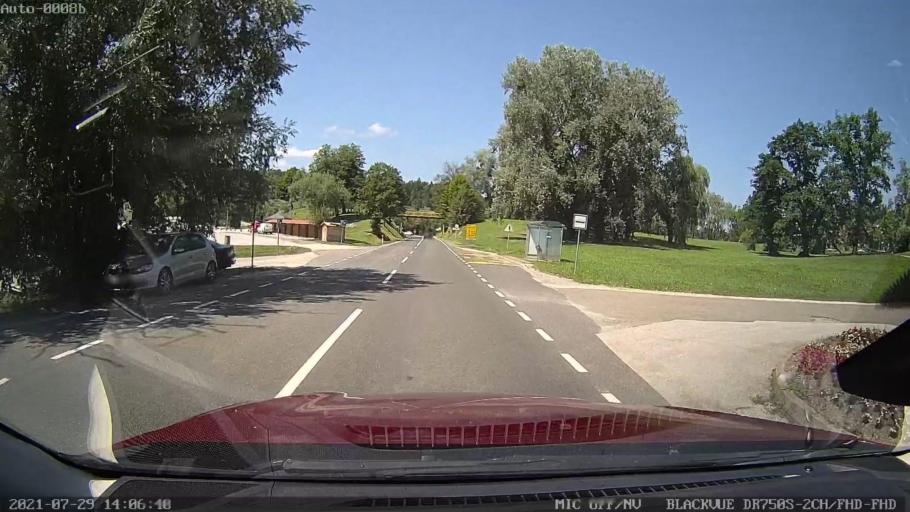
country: HR
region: Krapinsko-Zagorska
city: Radoboj
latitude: 46.2572
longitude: 15.9490
